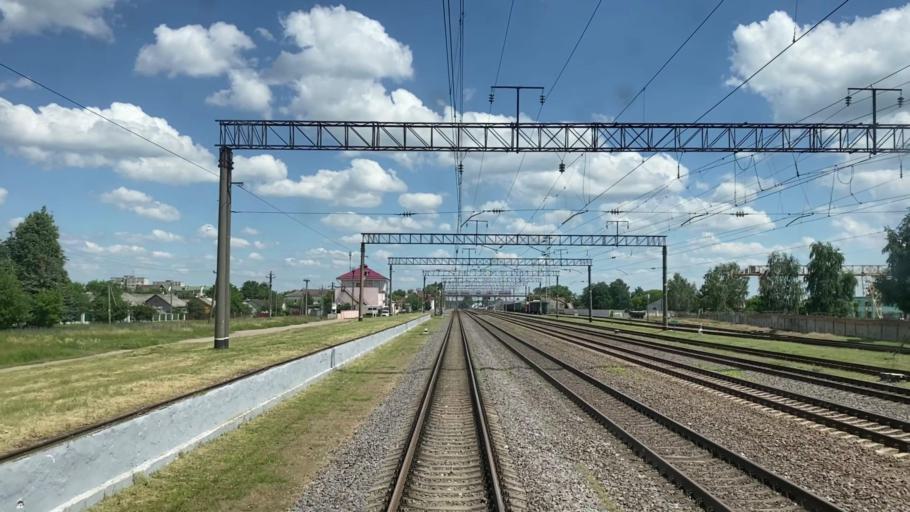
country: BY
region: Brest
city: Ivatsevichy
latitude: 52.7070
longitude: 25.3401
